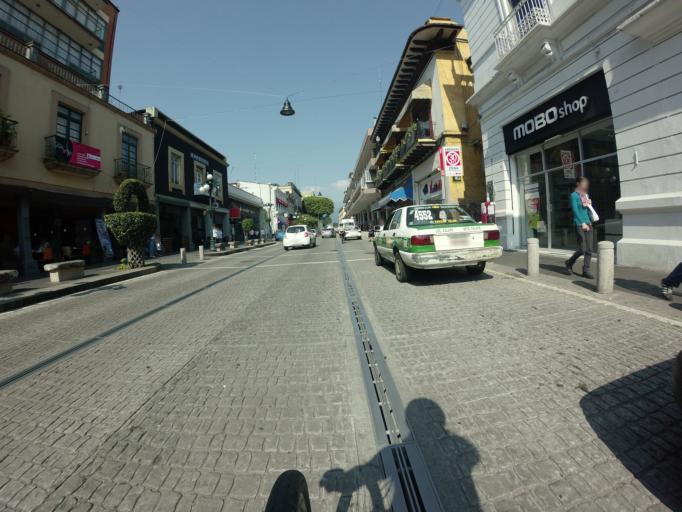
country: MX
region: Veracruz
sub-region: Xalapa
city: Xalapa de Enriquez
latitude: 19.5302
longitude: -96.9233
